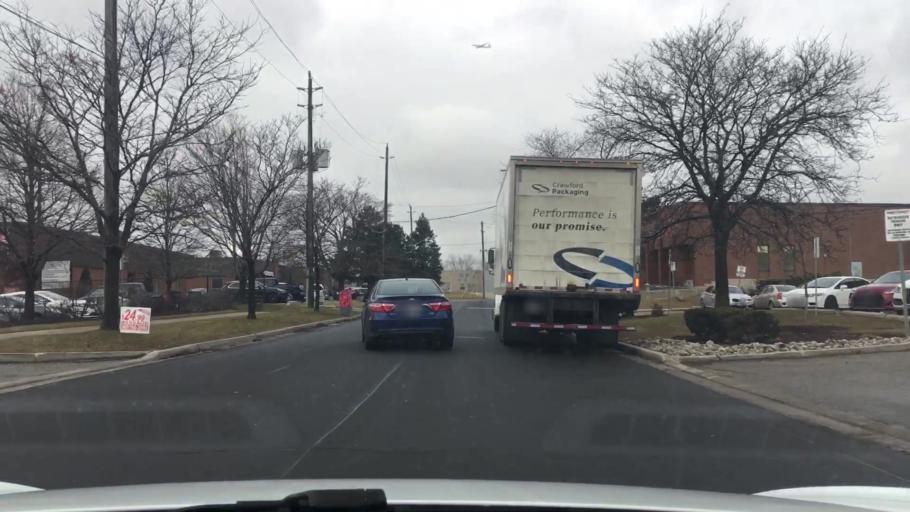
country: CA
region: Ontario
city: Willowdale
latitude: 43.8229
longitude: -79.3486
